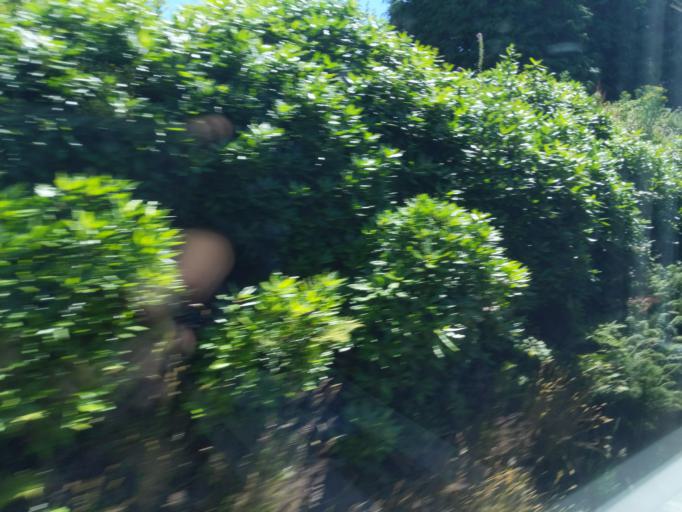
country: GB
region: England
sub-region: Cornwall
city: Redruth
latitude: 50.2504
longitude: -5.2085
